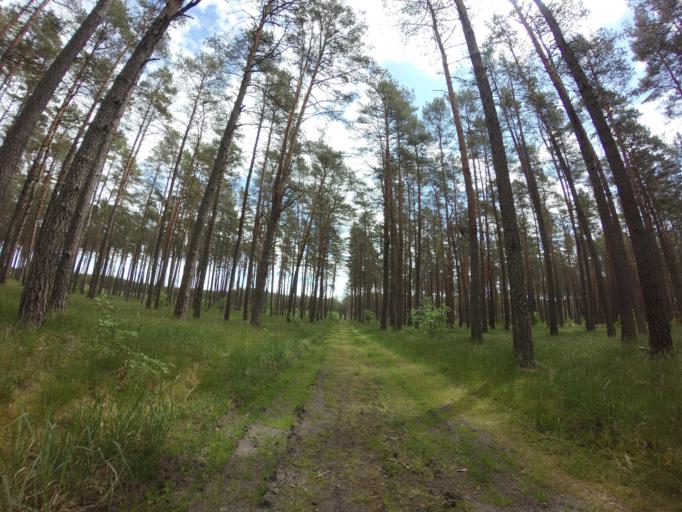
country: PL
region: West Pomeranian Voivodeship
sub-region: Powiat drawski
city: Kalisz Pomorski
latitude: 53.1602
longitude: 15.9710
